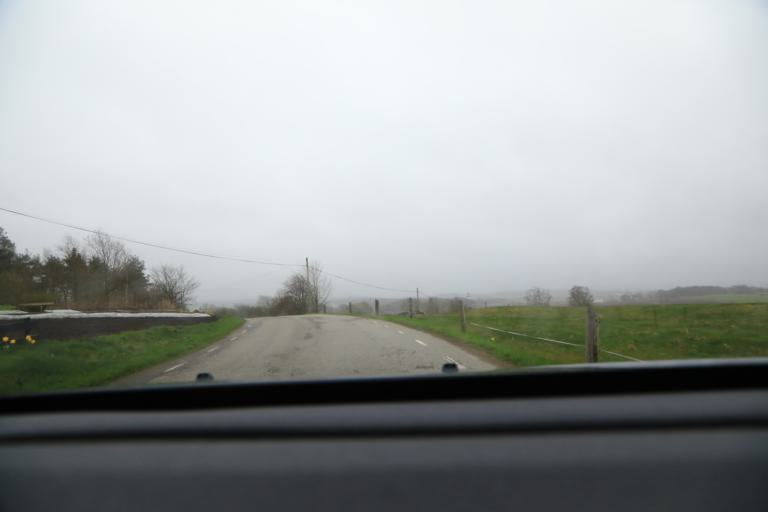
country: SE
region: Halland
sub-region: Kungsbacka Kommun
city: Frillesas
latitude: 57.2710
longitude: 12.1998
